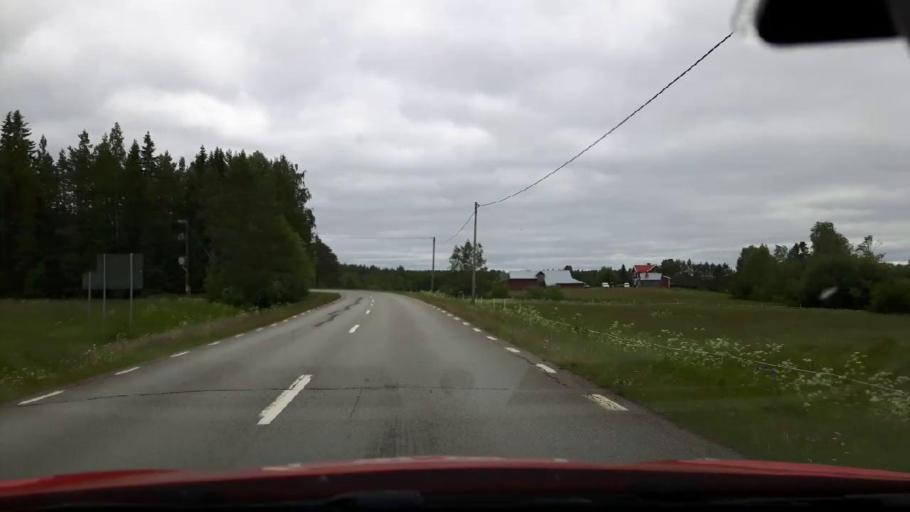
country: SE
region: Jaemtland
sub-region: Stroemsunds Kommun
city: Stroemsund
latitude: 63.5333
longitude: 15.4483
